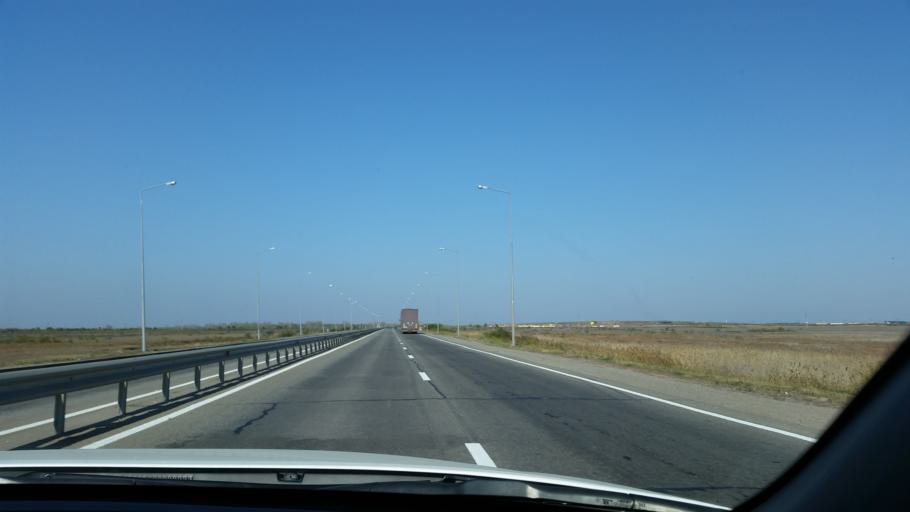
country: KZ
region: Astana Qalasy
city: Astana
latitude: 51.2397
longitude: 71.3331
